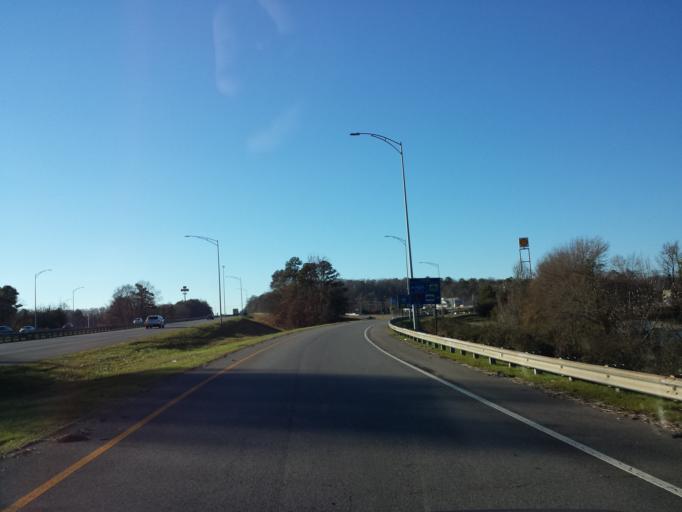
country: US
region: Alabama
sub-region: Tuscaloosa County
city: Holt
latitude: 33.1735
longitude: -87.4696
